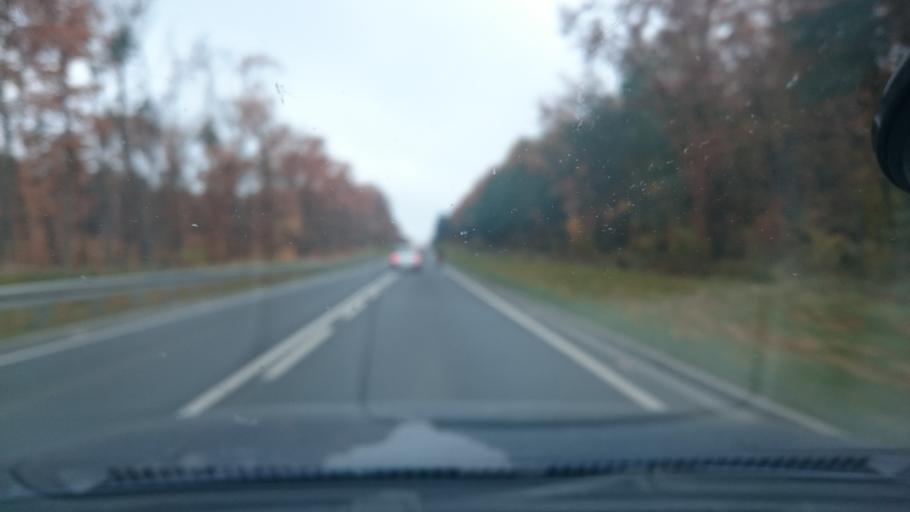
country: PL
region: Silesian Voivodeship
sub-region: Rybnik
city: Rybnik
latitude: 50.1103
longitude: 18.5640
